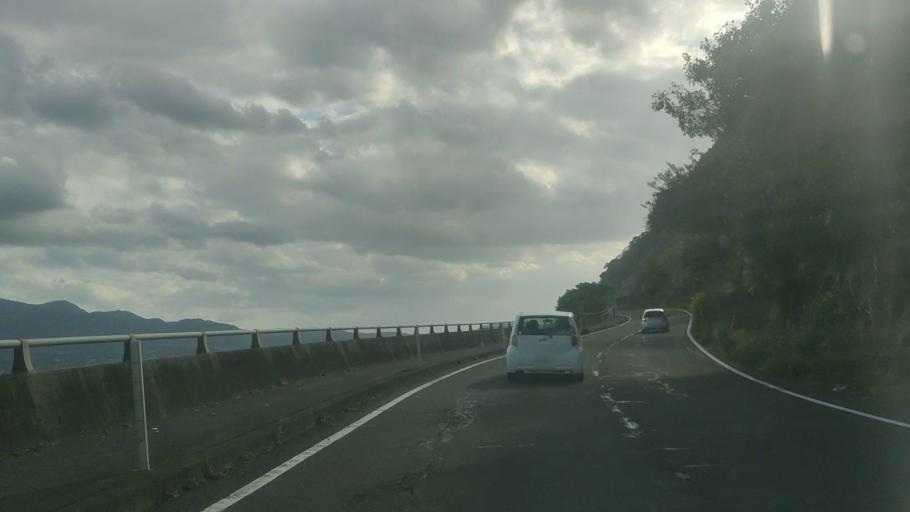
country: JP
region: Kagoshima
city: Kagoshima-shi
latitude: 31.6440
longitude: 130.6032
